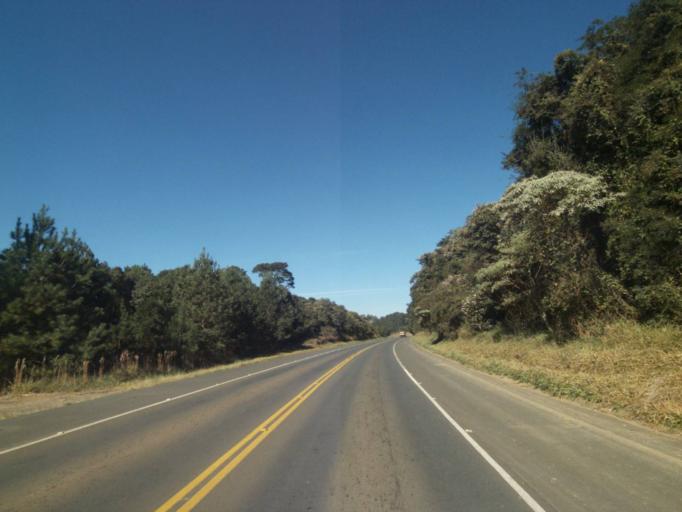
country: BR
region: Parana
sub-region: Tibagi
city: Tibagi
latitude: -24.5590
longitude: -50.4549
